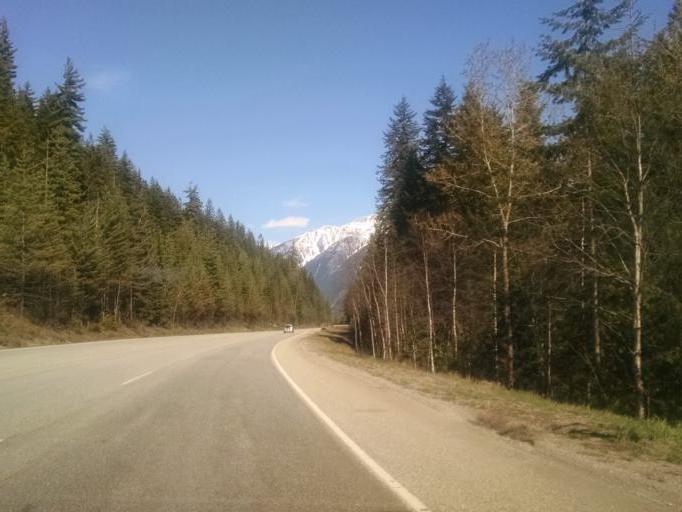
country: CA
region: British Columbia
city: Revelstoke
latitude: 51.0214
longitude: -118.0642
